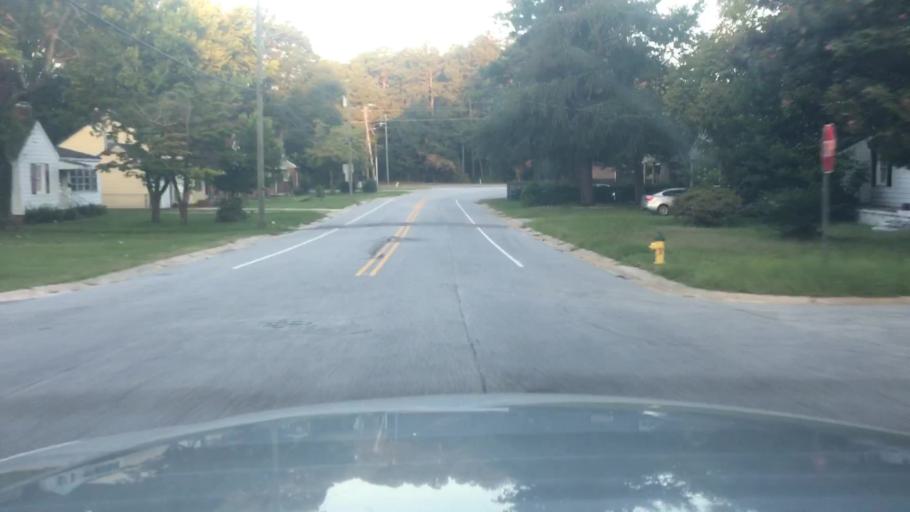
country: US
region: North Carolina
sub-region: Cumberland County
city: Fayetteville
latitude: 35.0857
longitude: -78.8786
